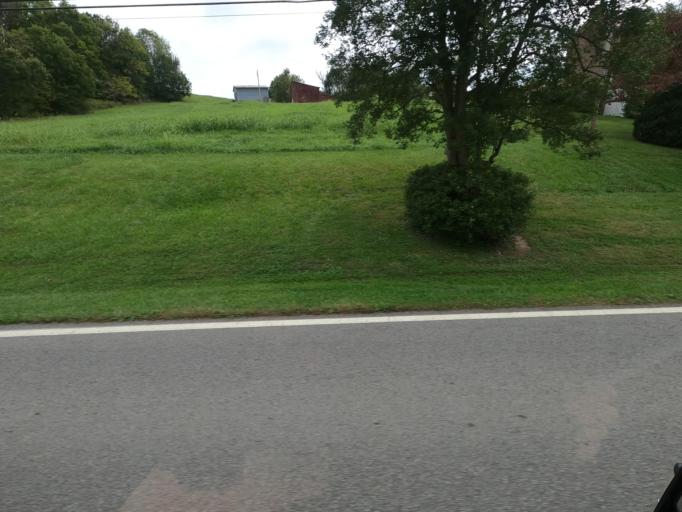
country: US
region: Tennessee
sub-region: Washington County
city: Jonesborough
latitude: 36.2225
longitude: -82.5681
